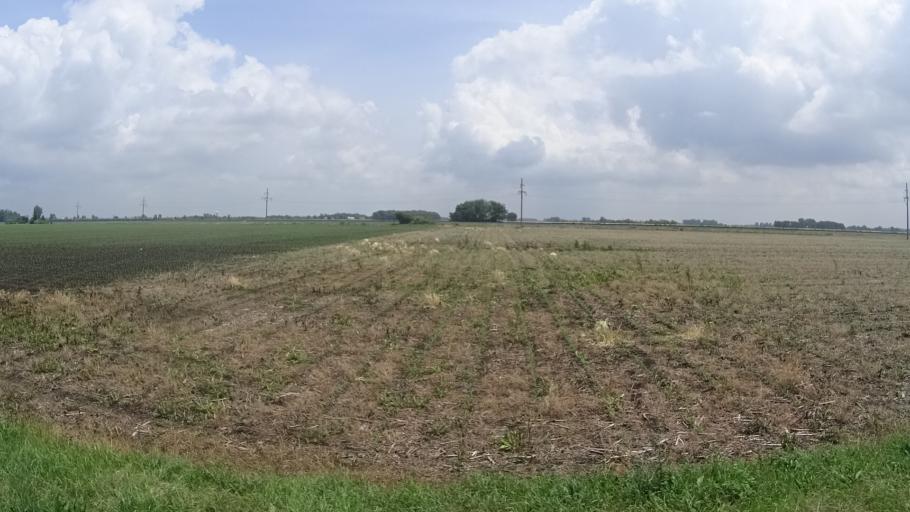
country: US
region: Ohio
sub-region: Huron County
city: Bellevue
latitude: 41.3192
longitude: -82.8052
